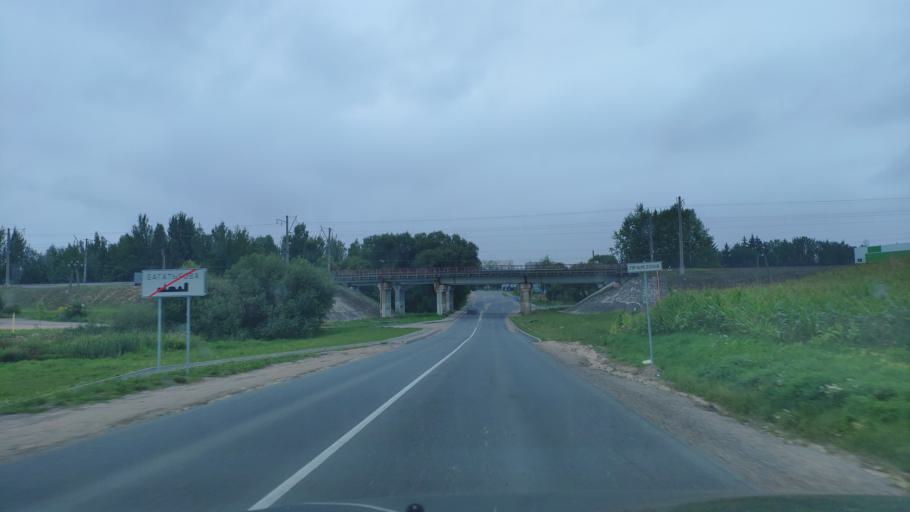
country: BY
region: Minsk
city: Azyartso
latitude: 53.8442
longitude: 27.4100
